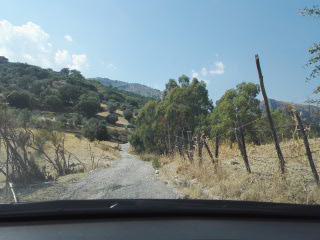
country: IT
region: Calabria
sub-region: Provincia di Reggio Calabria
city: Stilo
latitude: 38.4562
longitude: 16.4645
